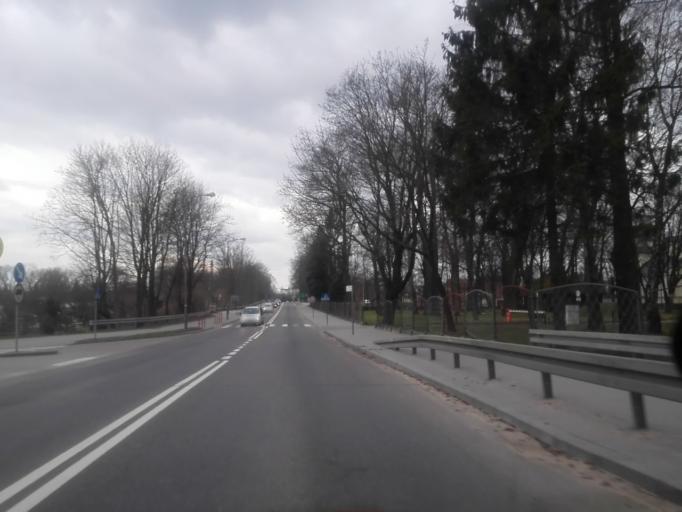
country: PL
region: Podlasie
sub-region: Powiat augustowski
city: Augustow
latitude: 53.8432
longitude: 22.9946
